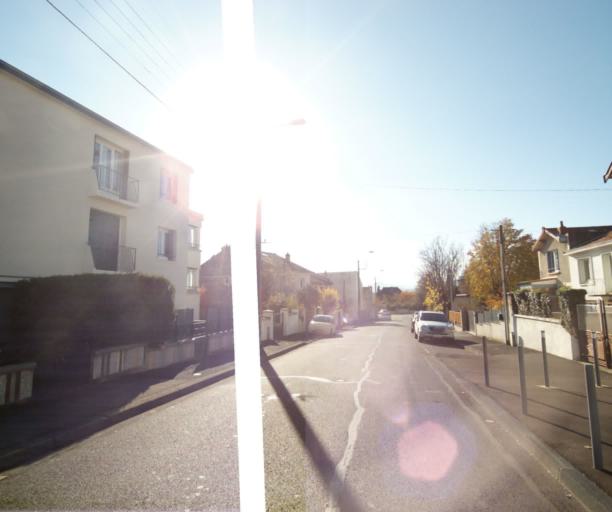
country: FR
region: Auvergne
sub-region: Departement du Puy-de-Dome
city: Clermont-Ferrand
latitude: 45.7935
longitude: 3.0826
